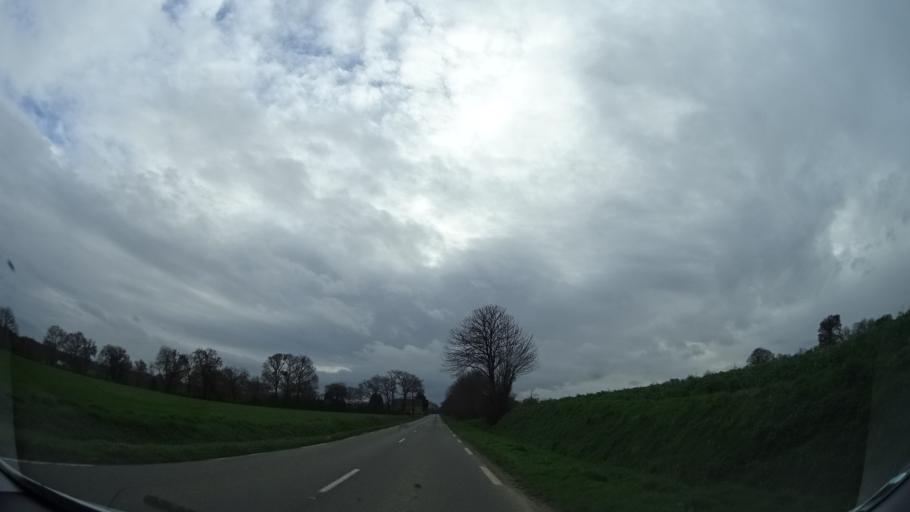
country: FR
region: Brittany
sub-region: Departement des Cotes-d'Armor
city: Evran
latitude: 48.3482
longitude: -1.9683
